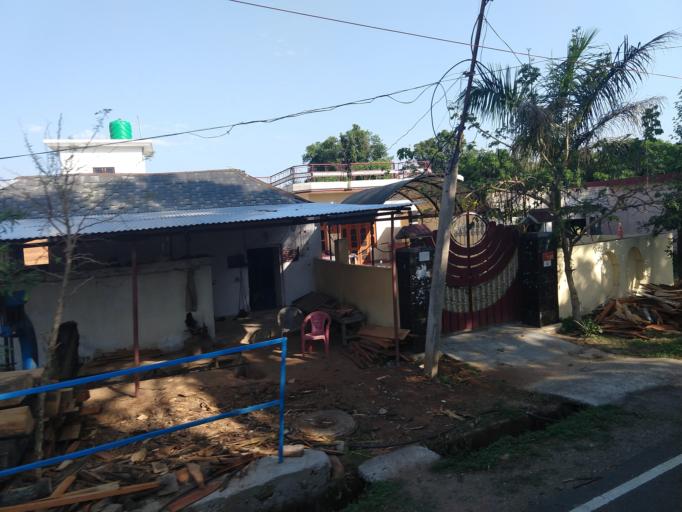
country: IN
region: Himachal Pradesh
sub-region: Chamba
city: Chowari
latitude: 32.3552
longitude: 75.9190
